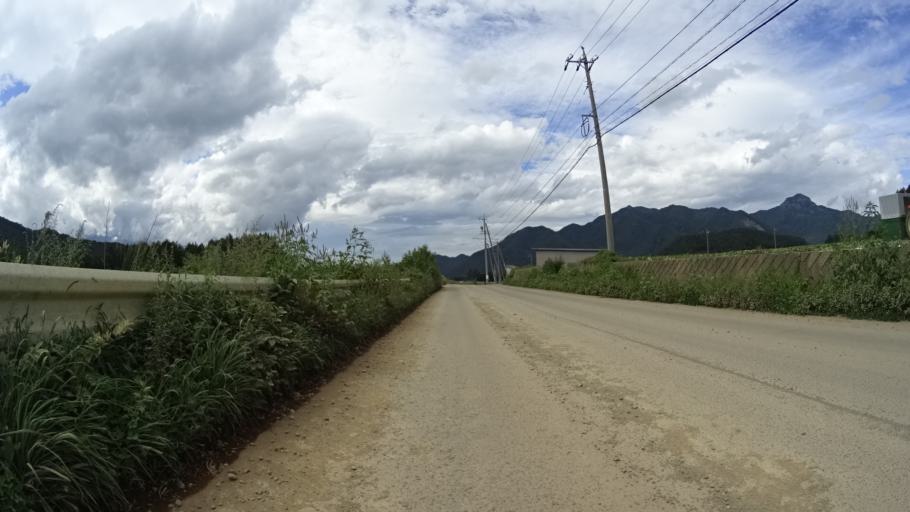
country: JP
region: Yamanashi
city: Nirasaki
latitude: 35.9516
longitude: 138.5477
